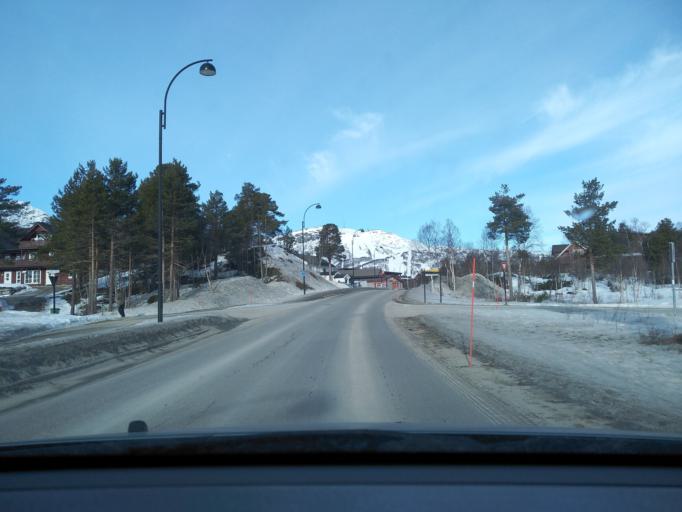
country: NO
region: Aust-Agder
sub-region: Bykle
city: Hovden
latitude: 59.5581
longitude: 7.3579
